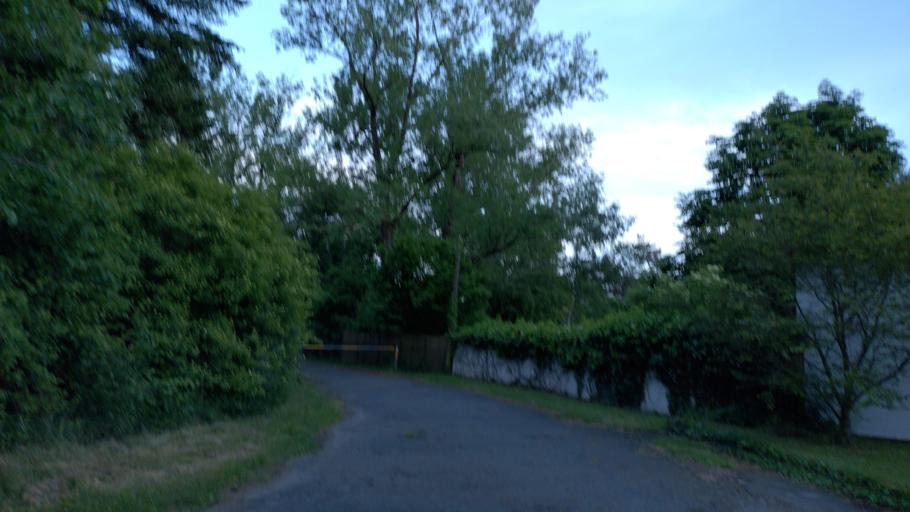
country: DE
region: Bavaria
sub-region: Upper Franconia
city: Bindlach
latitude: 49.9951
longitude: 11.6172
